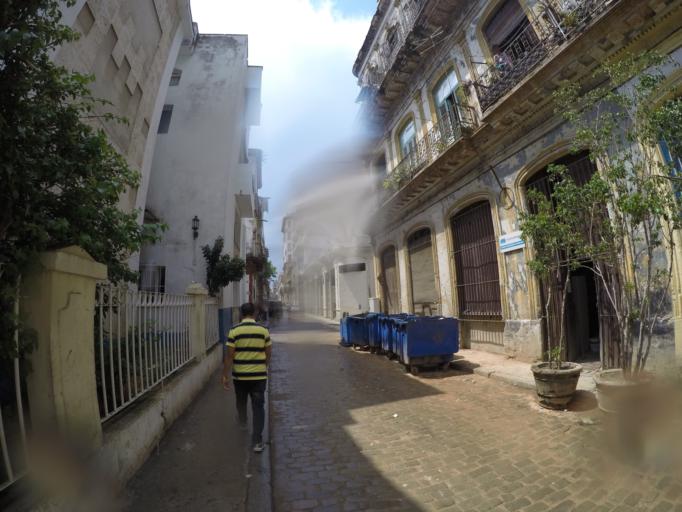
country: CU
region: La Habana
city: La Habana Vieja
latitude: 23.1353
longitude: -82.3507
